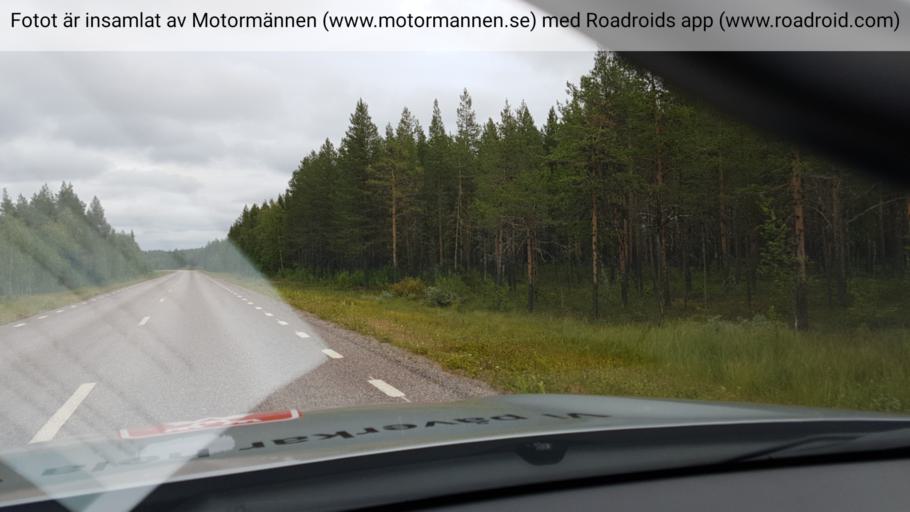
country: SE
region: Norrbotten
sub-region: Gallivare Kommun
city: Gaellivare
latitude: 67.0582
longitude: 21.2543
